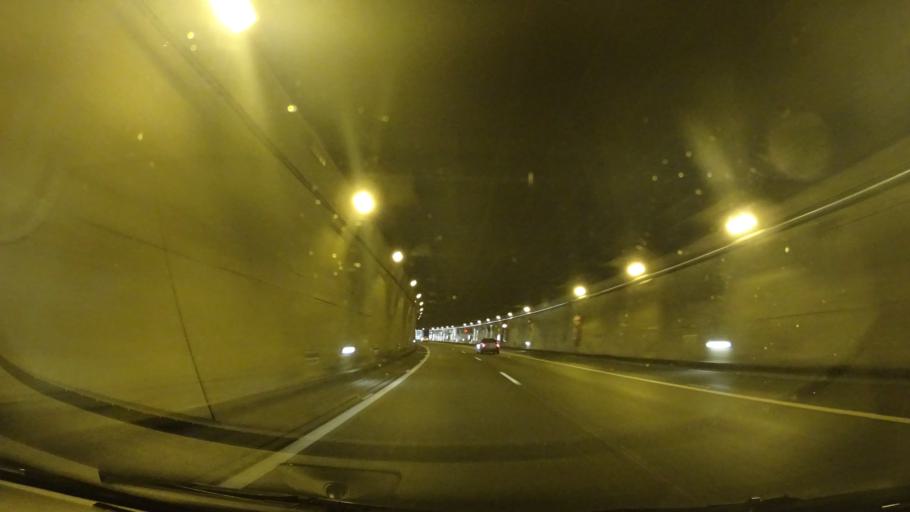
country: ES
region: Madrid
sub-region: Provincia de Madrid
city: Guadarrama
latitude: 40.7168
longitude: -4.1587
